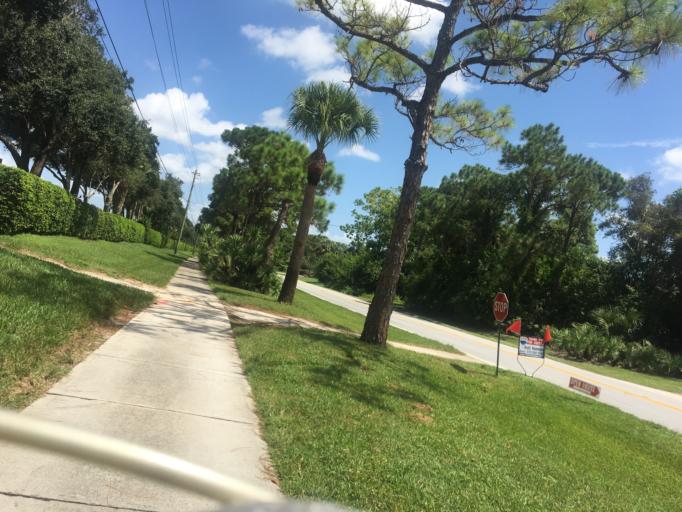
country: US
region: Florida
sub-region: Martin County
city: Palm City
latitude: 27.1530
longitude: -80.2698
